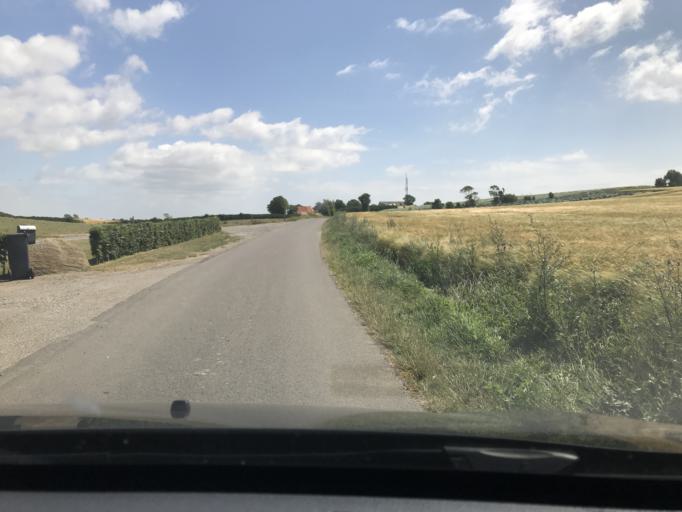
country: DK
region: South Denmark
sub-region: AEro Kommune
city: AEroskobing
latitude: 54.9058
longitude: 10.3036
